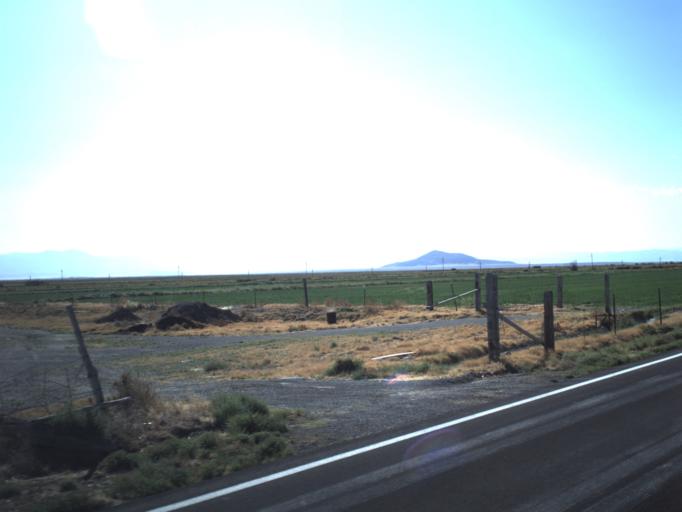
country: US
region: Utah
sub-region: Millard County
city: Delta
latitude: 39.2656
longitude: -112.6532
